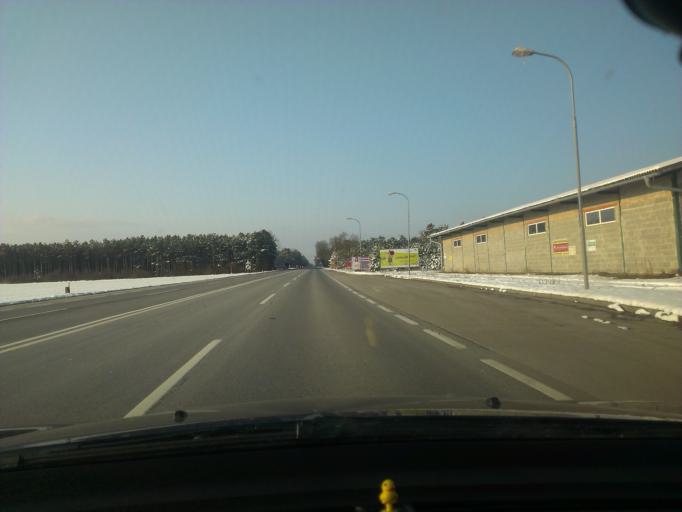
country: AT
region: Lower Austria
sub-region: Politischer Bezirk Wiener Neustadt
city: Weikersdorf am Steinfelde
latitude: 47.7801
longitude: 16.1900
